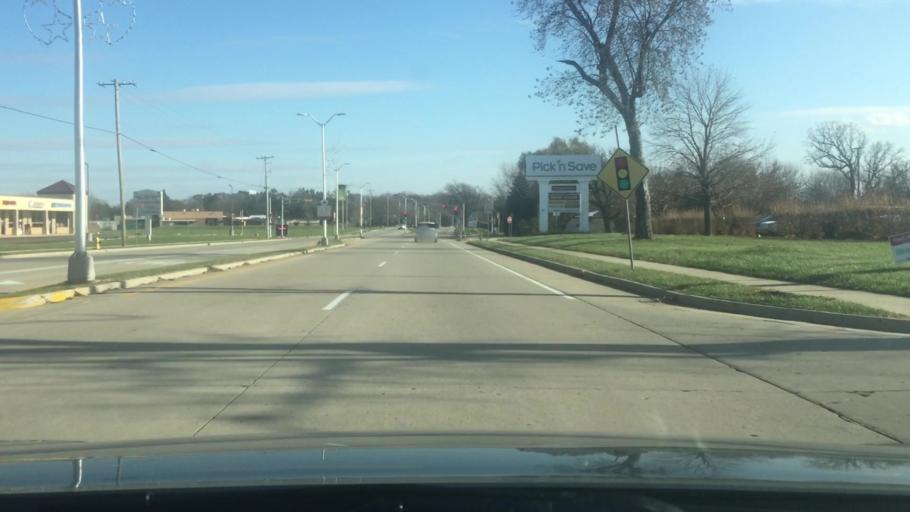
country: US
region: Wisconsin
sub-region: Jefferson County
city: Fort Atkinson
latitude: 42.9409
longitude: -88.8604
